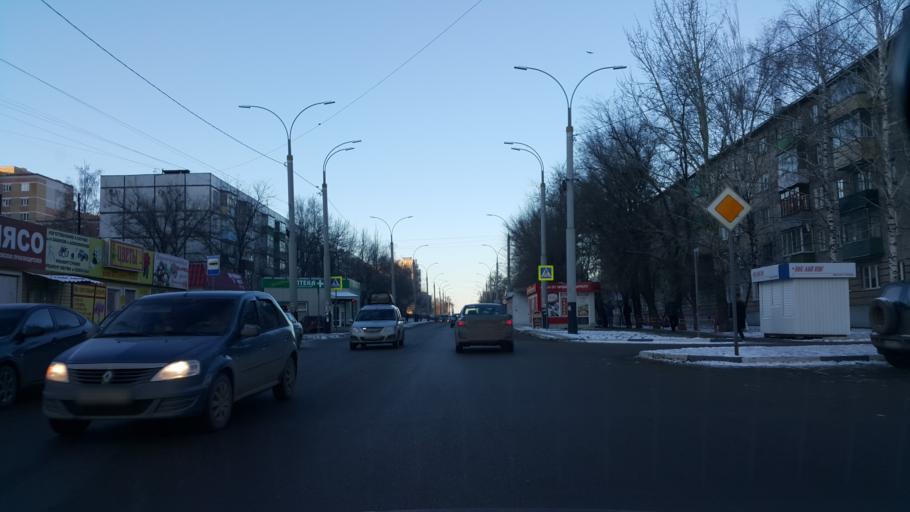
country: RU
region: Tambov
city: Pokrovo-Prigorodnoye
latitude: 52.7048
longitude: 41.3993
